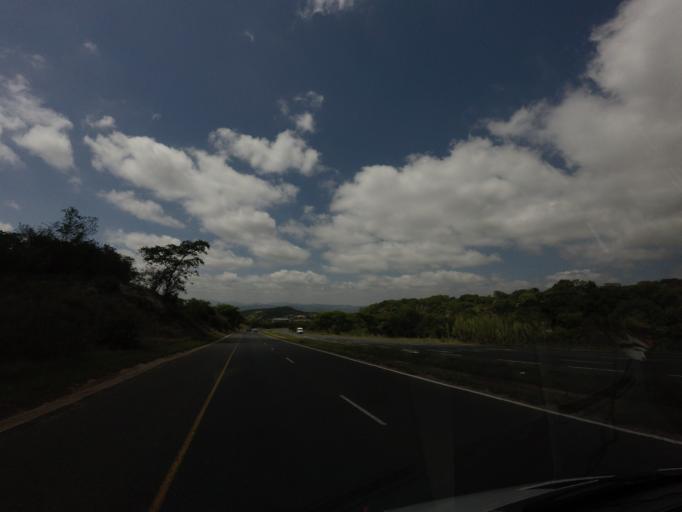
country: ZA
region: Mpumalanga
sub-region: Ehlanzeni District
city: White River
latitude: -25.3973
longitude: 30.9824
